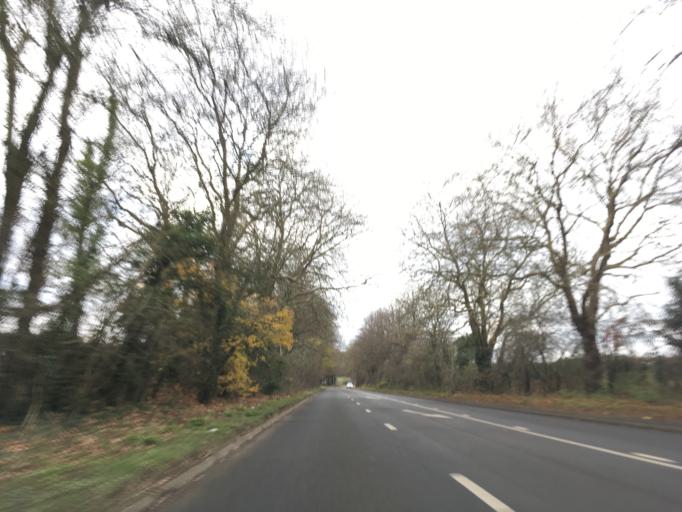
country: GB
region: Wales
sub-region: Monmouthshire
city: Rogiet
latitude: 51.6138
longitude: -2.7745
